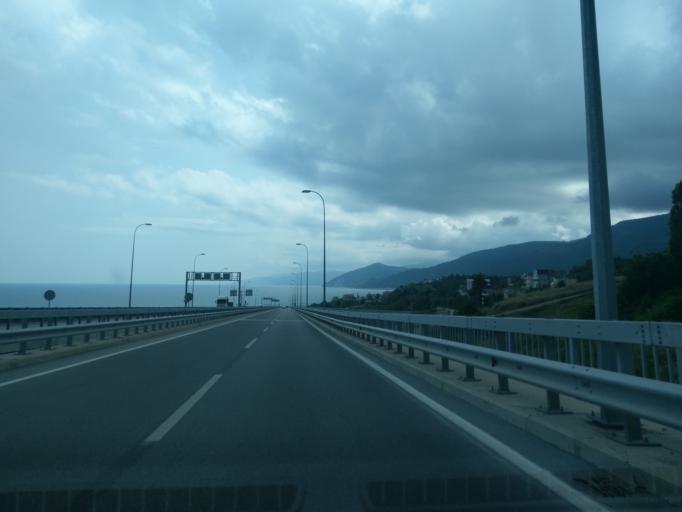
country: TR
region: Sinop
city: Gerze
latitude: 41.7868
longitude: 35.1936
